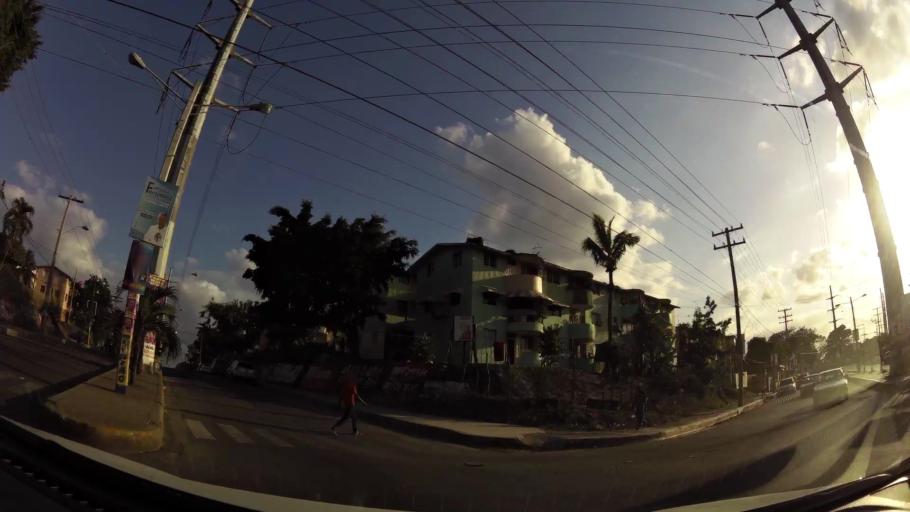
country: DO
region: Nacional
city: La Agustina
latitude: 18.5443
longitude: -69.9291
